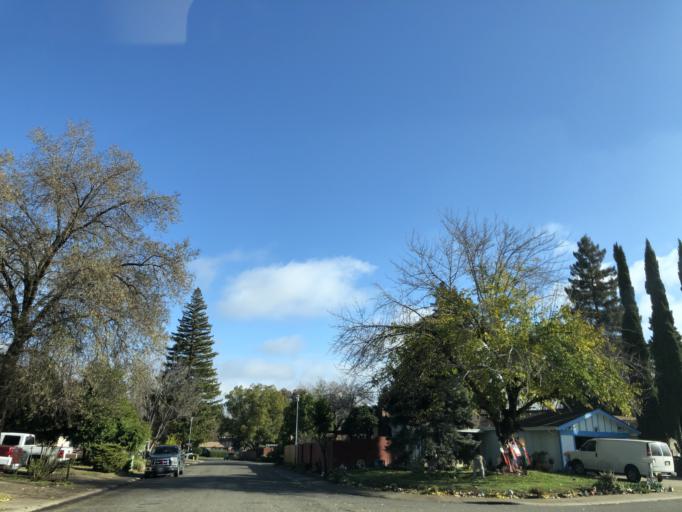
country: US
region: California
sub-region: Sacramento County
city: Rosemont
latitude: 38.5624
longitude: -121.3802
